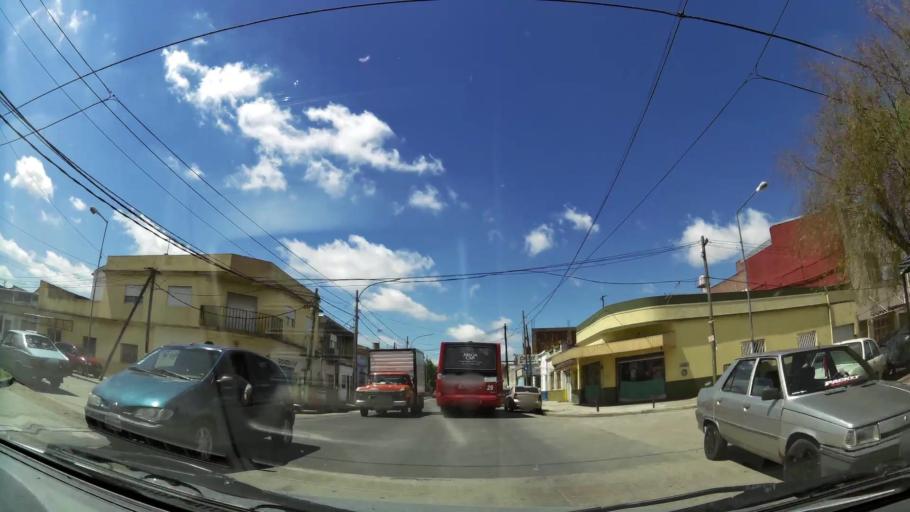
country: AR
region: Buenos Aires
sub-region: Partido de Lanus
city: Lanus
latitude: -34.6936
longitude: -58.4244
